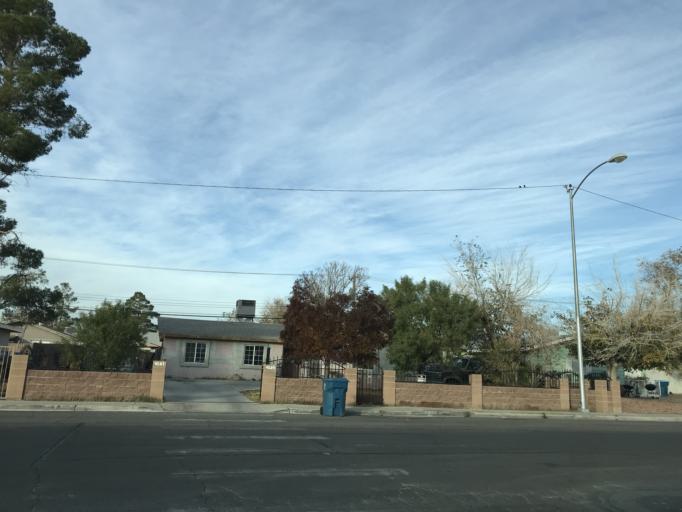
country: US
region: Nevada
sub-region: Clark County
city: Nellis Air Force Base
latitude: 36.2366
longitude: -115.0711
